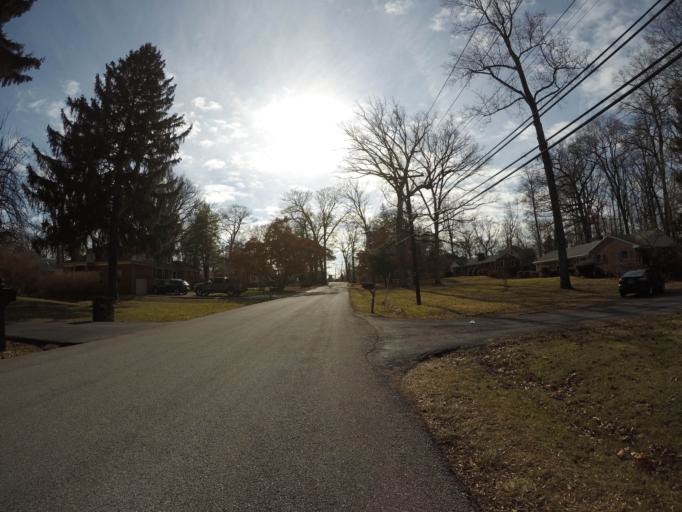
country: US
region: Maryland
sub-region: Howard County
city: Columbia
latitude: 39.2705
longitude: -76.8326
